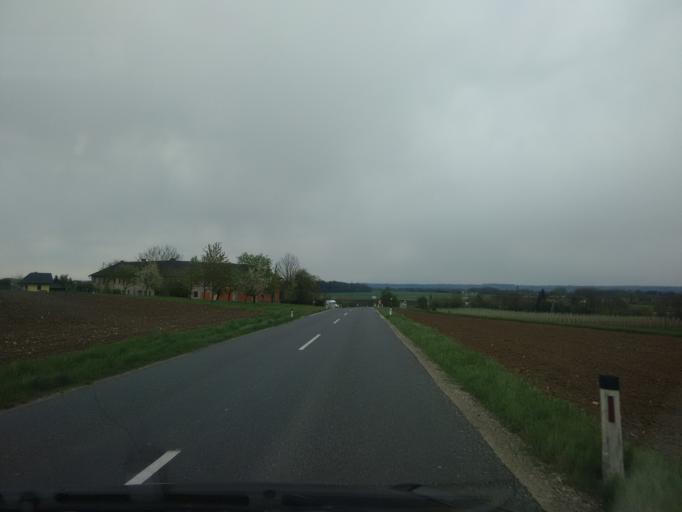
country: AT
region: Upper Austria
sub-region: Wels-Land
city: Holzhausen
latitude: 48.2175
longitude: 14.0818
